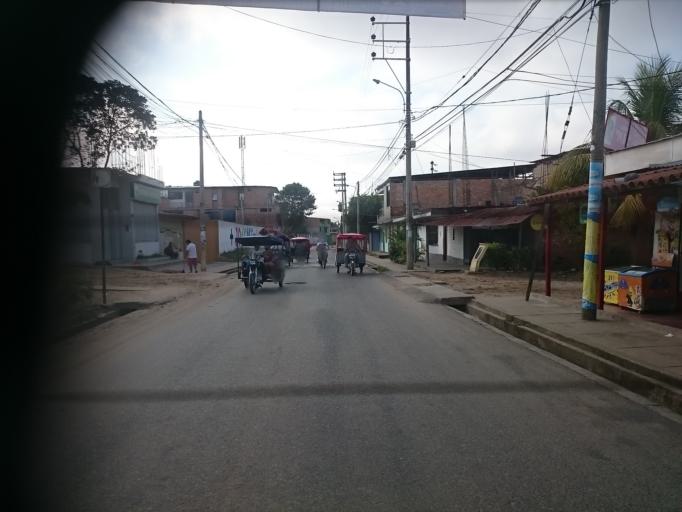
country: PE
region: San Martin
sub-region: Provincia de San Martin
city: Tarapoto
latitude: -6.4803
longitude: -76.3784
